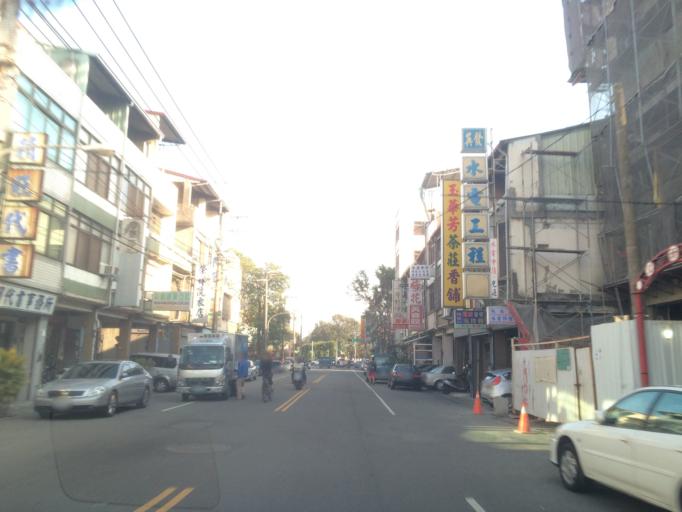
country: TW
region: Taiwan
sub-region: Taichung City
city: Taichung
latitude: 24.1913
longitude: 120.6838
